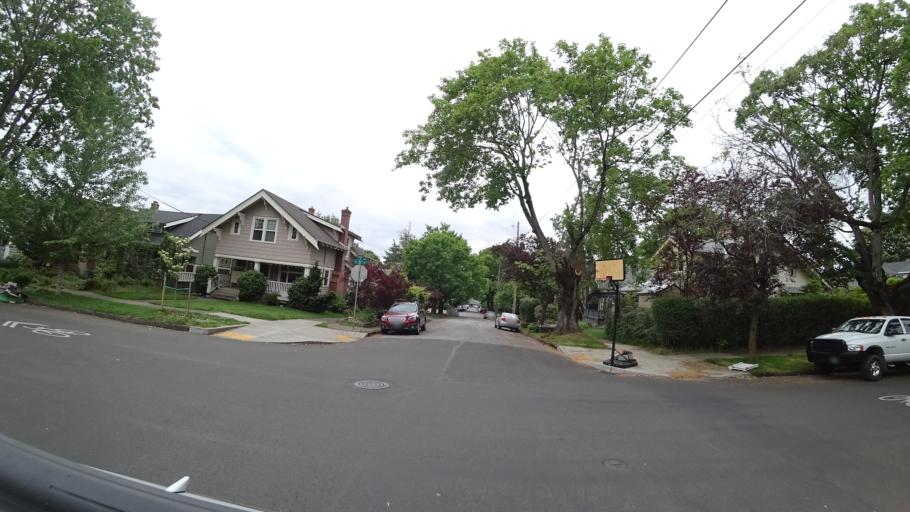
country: US
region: Oregon
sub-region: Multnomah County
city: Lents
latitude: 45.5129
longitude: -122.6093
